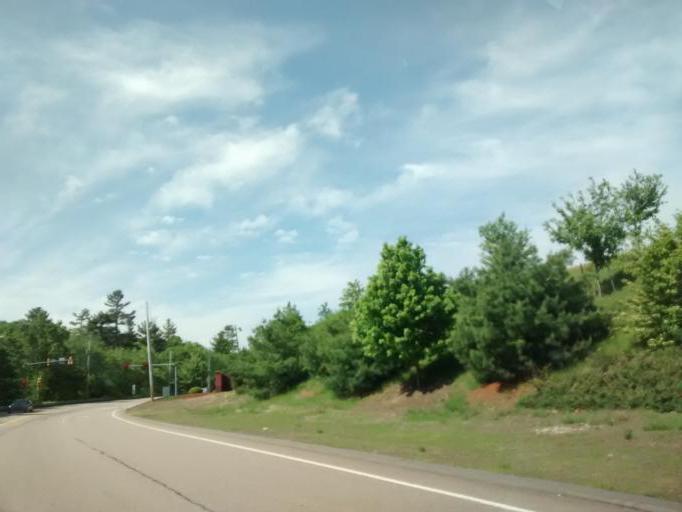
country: US
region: Massachusetts
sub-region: Worcester County
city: Whitinsville
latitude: 42.1059
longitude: -71.6987
